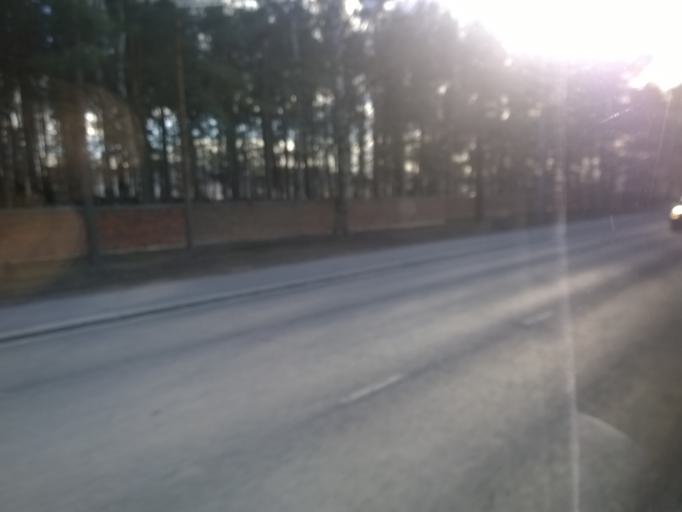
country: FI
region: Pirkanmaa
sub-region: Tampere
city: Tampere
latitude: 61.4952
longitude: 23.7877
